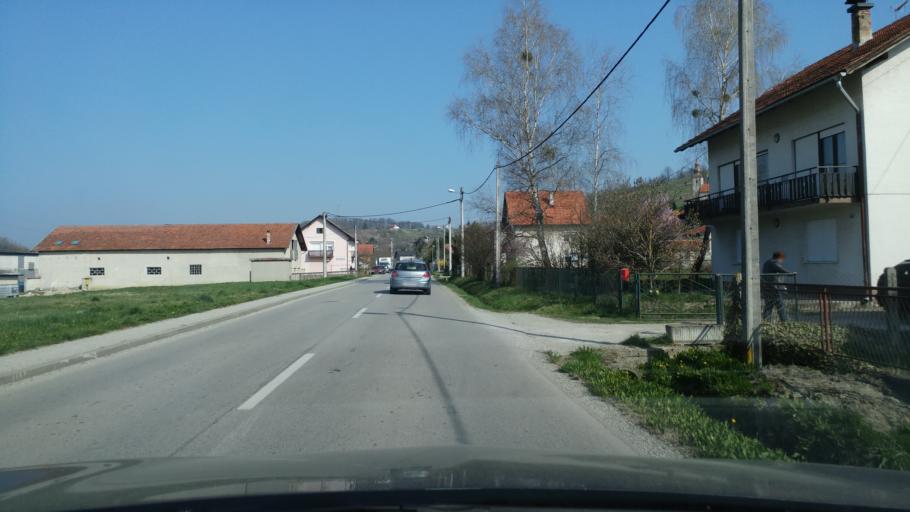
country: HR
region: Zagrebacka
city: Pojatno
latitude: 45.9099
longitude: 15.7802
